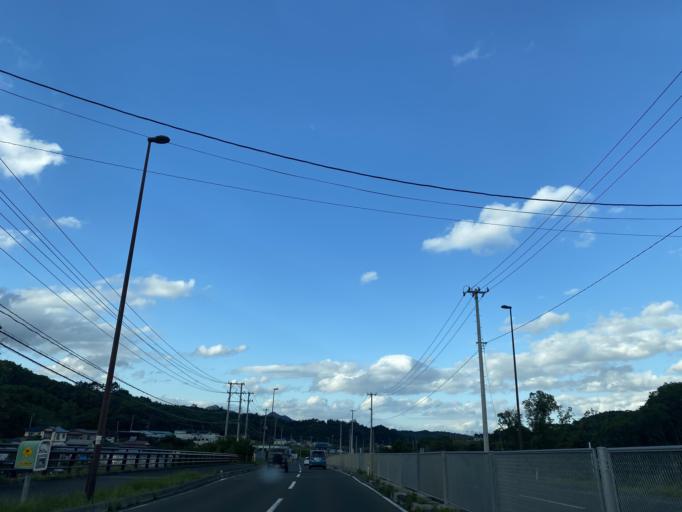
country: JP
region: Miyagi
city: Tomiya
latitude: 38.3729
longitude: 140.8557
